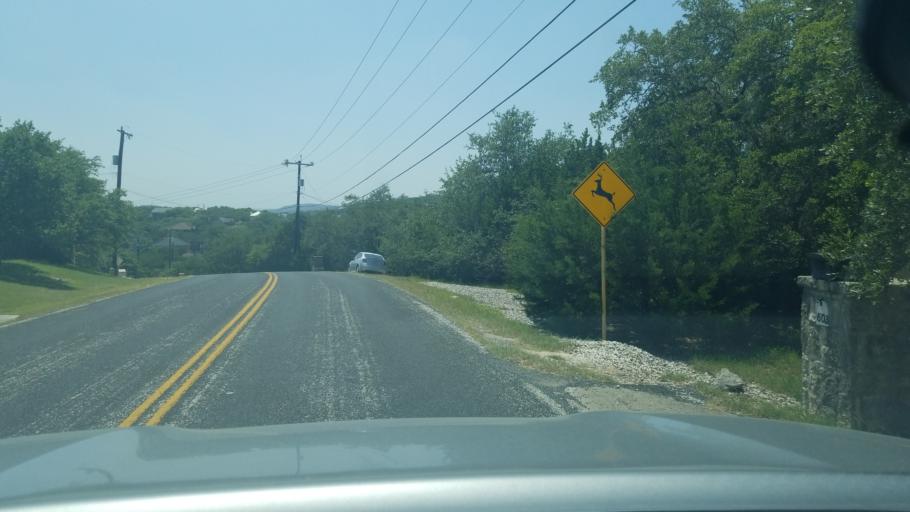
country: US
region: Texas
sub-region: Bexar County
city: Timberwood Park
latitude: 29.6813
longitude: -98.5040
